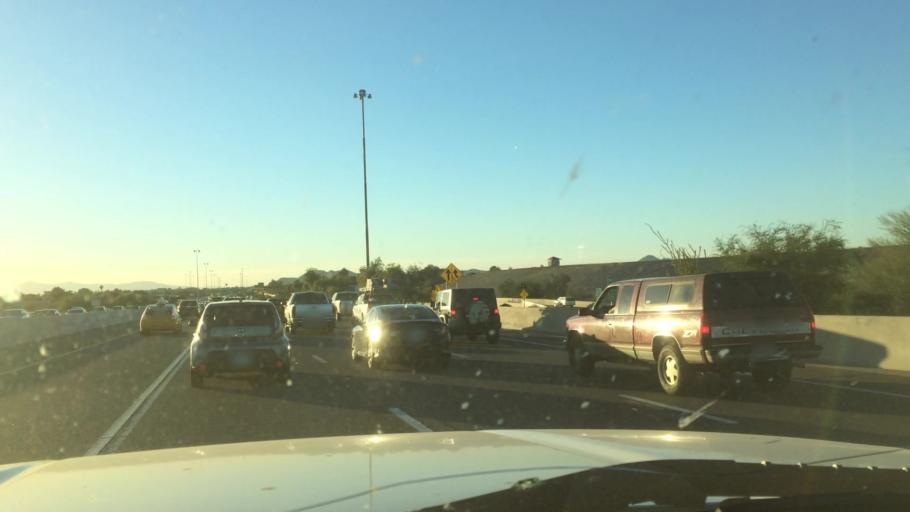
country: US
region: Arizona
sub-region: Maricopa County
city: Glendale
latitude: 33.6700
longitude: -112.0691
